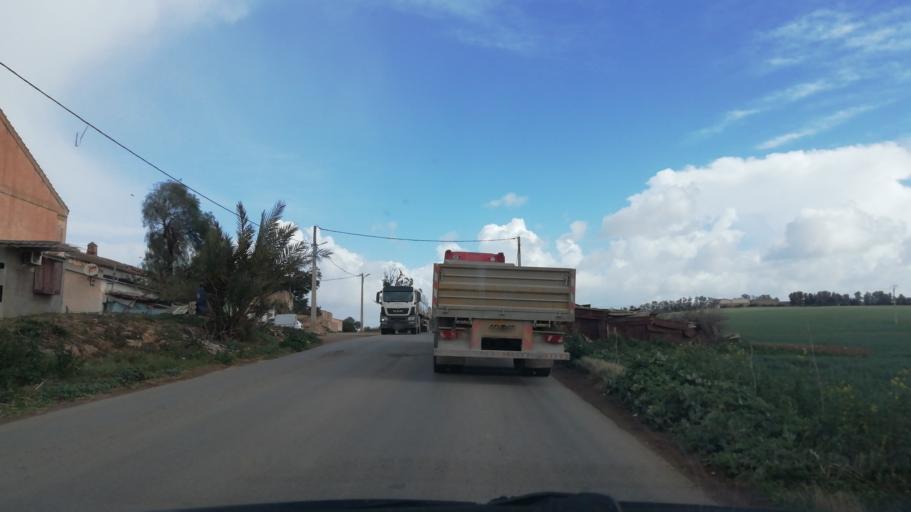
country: DZ
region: Oran
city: Sidi ech Chahmi
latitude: 35.6418
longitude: -0.5166
